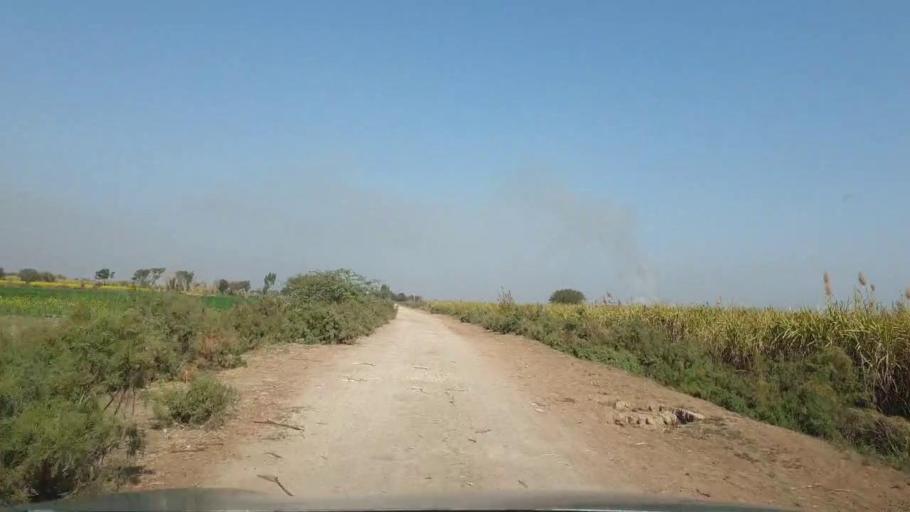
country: PK
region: Sindh
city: Mirpur Khas
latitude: 25.6413
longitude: 68.8967
